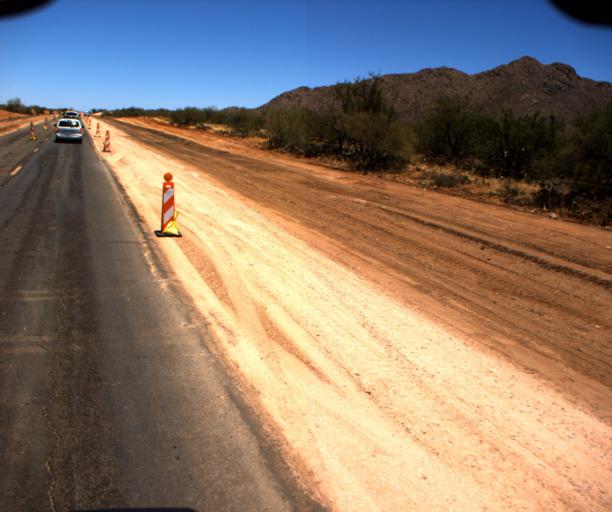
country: US
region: Arizona
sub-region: Pima County
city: Sells
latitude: 32.0022
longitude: -111.6857
